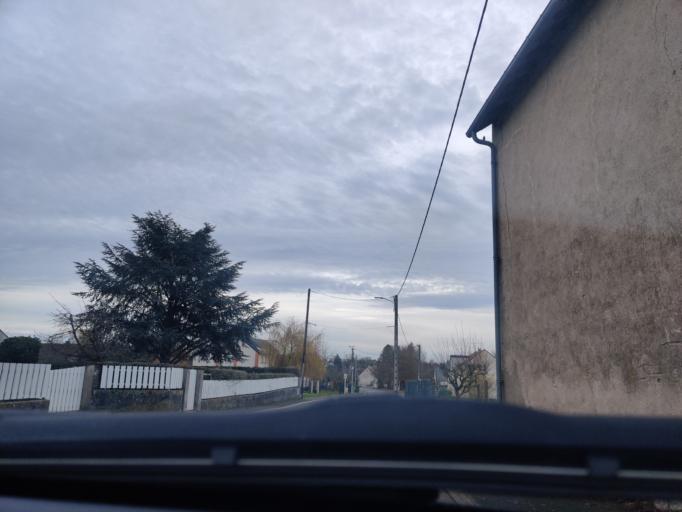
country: FR
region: Centre
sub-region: Departement du Loiret
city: La Chapelle-Saint-Mesmin
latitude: 47.8905
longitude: 1.8284
